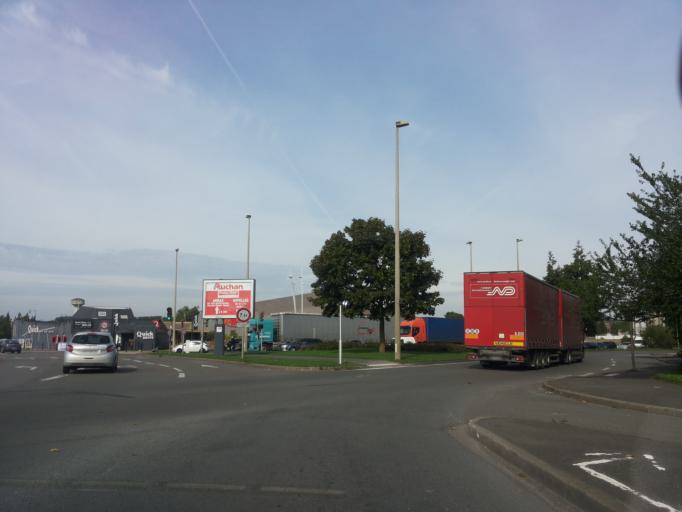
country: FR
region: Nord-Pas-de-Calais
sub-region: Departement du Pas-de-Calais
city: Arras
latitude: 50.2965
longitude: 2.7839
